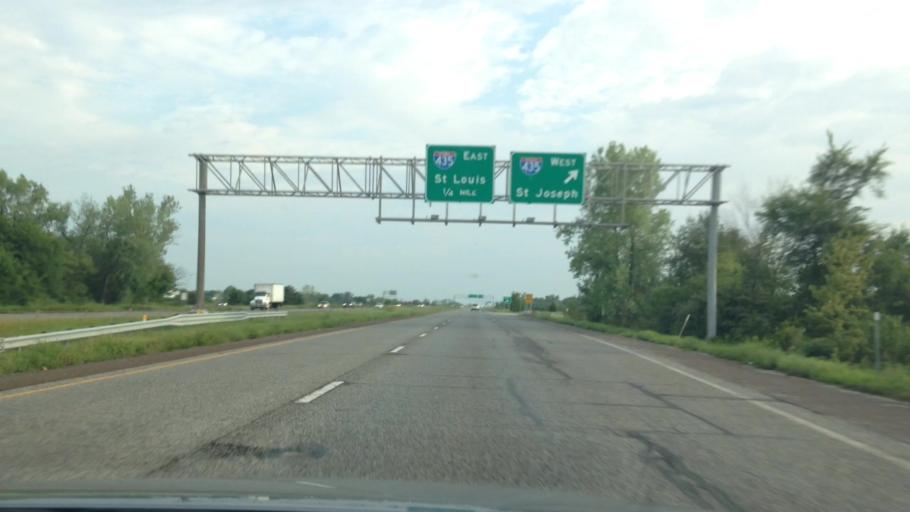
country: US
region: Missouri
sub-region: Clay County
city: Smithville
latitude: 39.3153
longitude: -94.5846
